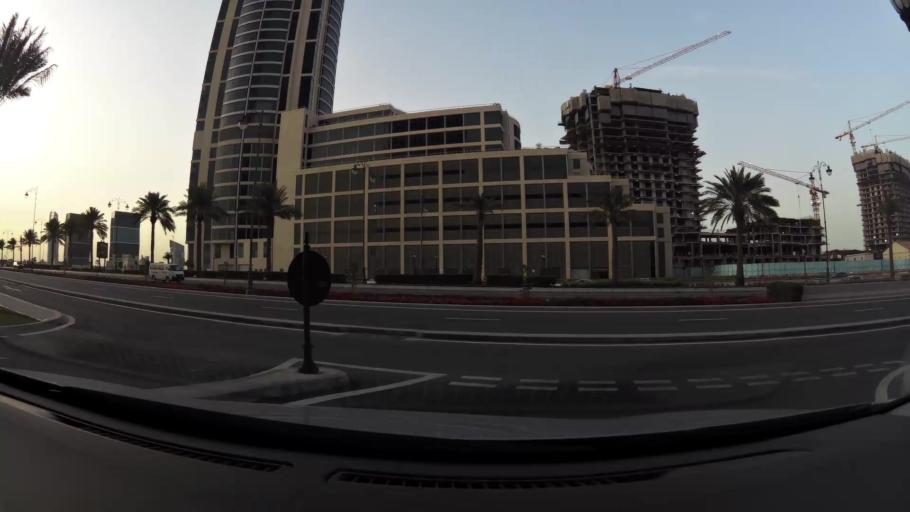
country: QA
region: Baladiyat ad Dawhah
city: Doha
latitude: 25.3716
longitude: 51.5342
